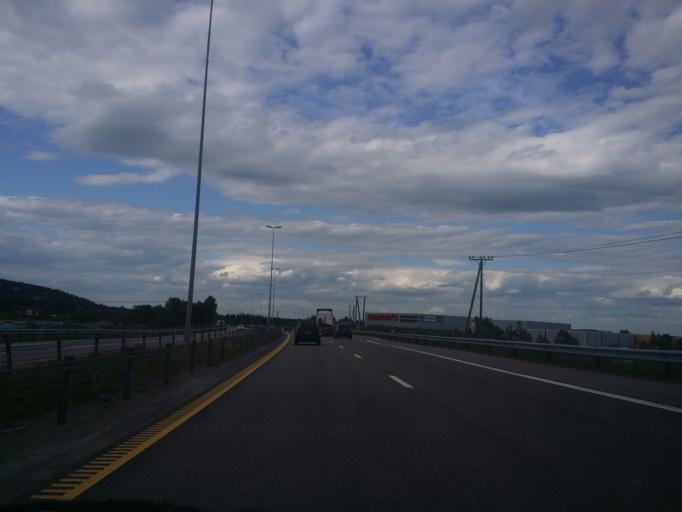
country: NO
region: Akershus
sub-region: Skedsmo
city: Leirsund
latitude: 60.0127
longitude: 11.0628
